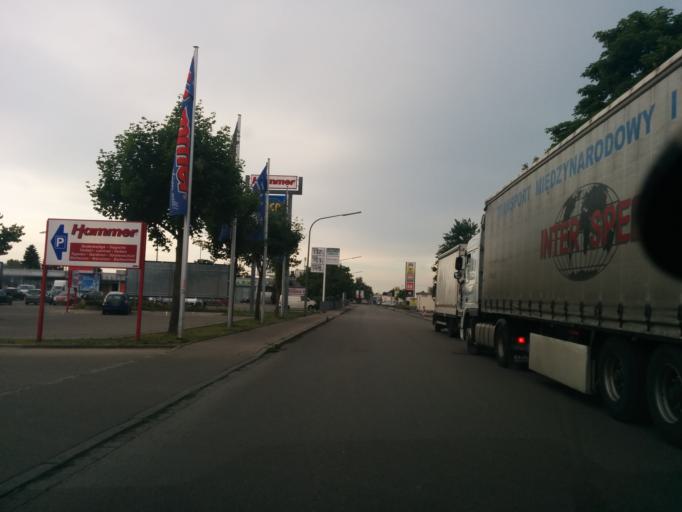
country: DE
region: Bavaria
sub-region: Swabia
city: Konigsbrunn
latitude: 48.2859
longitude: 10.8917
